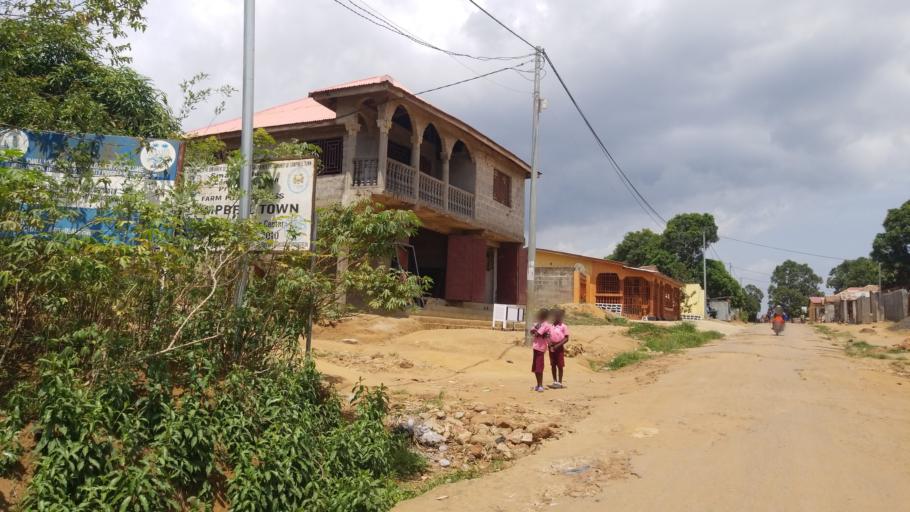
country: SL
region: Western Area
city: Waterloo
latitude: 8.3157
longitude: -13.0570
